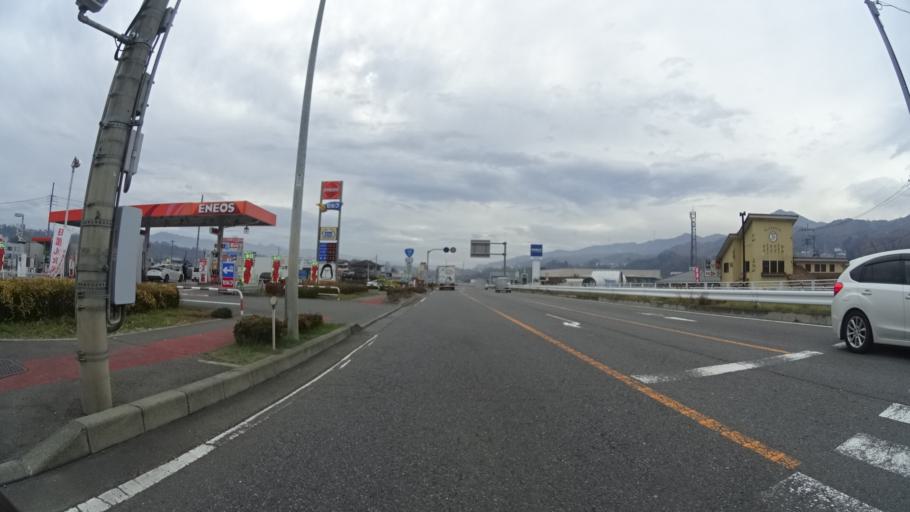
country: JP
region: Gunma
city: Numata
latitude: 36.6445
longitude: 139.0288
